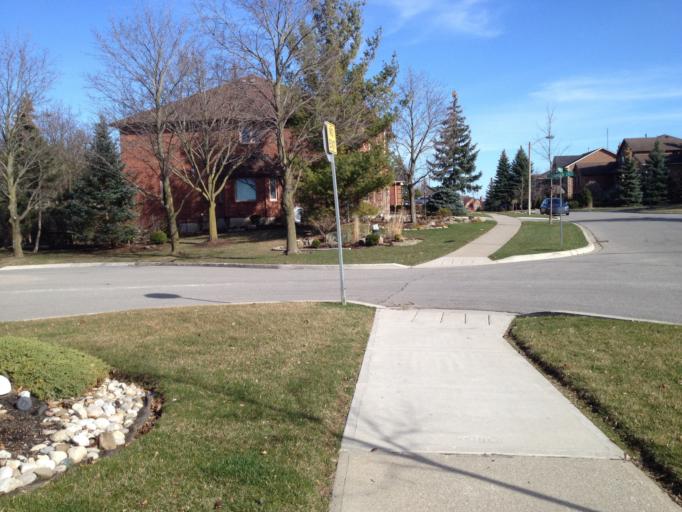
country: CA
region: Ontario
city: Brampton
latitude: 43.7429
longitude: -79.8104
